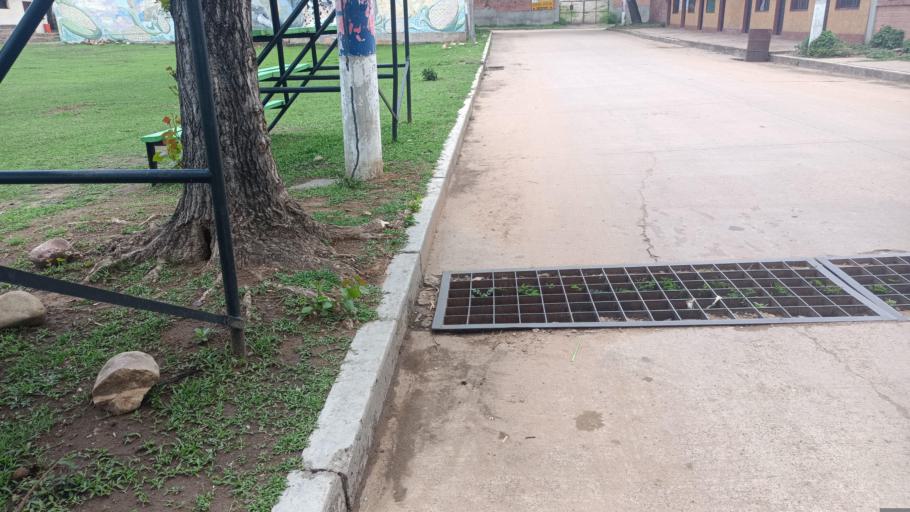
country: BO
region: Tarija
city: Entre Rios
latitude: -21.5299
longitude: -64.1729
